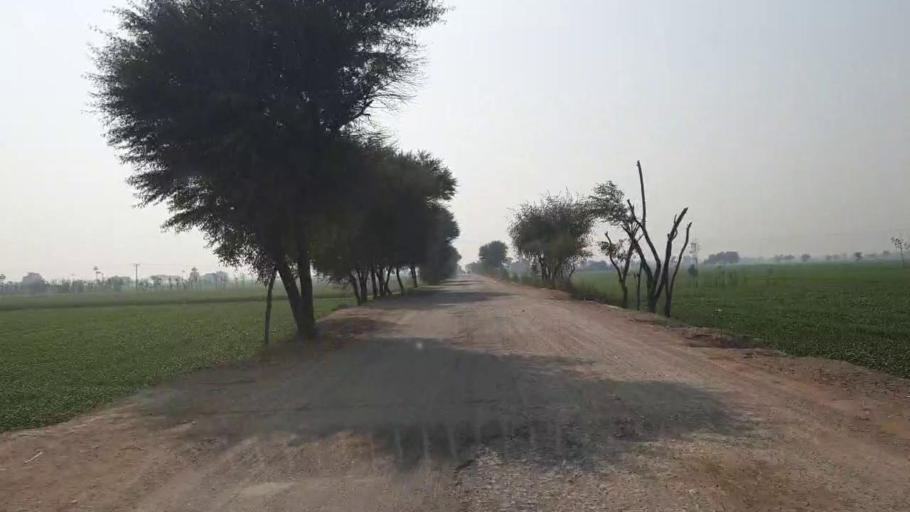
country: PK
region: Sindh
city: Hala
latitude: 25.8821
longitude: 68.4363
